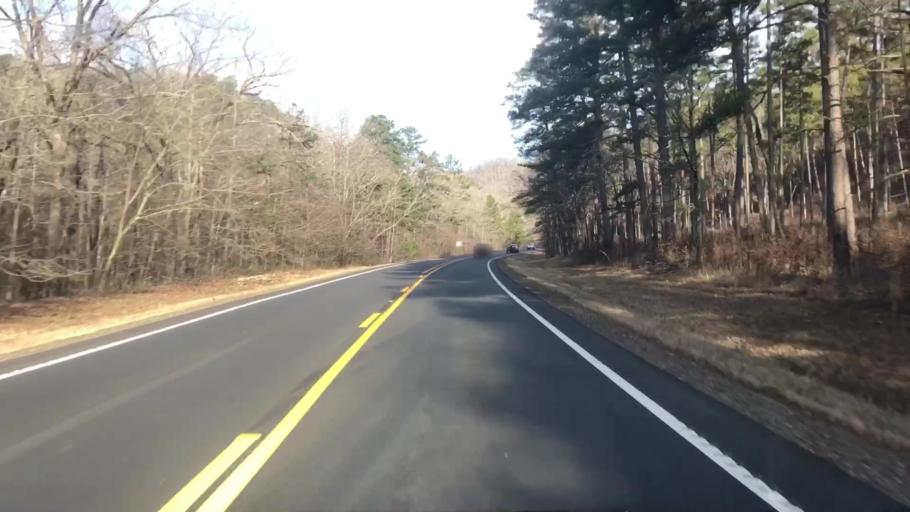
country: US
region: Arkansas
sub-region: Montgomery County
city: Mount Ida
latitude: 34.5195
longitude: -93.3885
